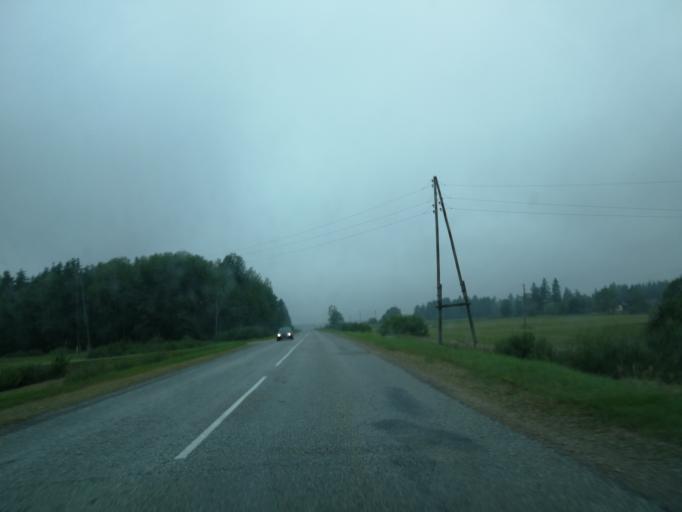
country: LV
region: Varkava
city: Vecvarkava
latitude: 56.3134
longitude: 26.5280
